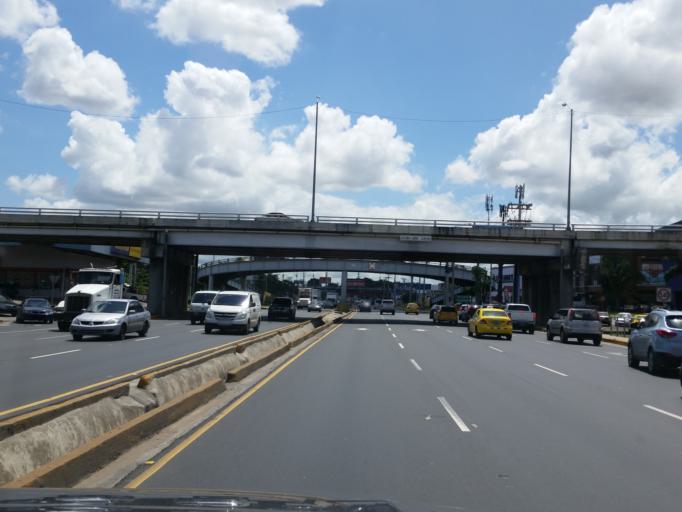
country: PA
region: Panama
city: San Miguelito
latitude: 9.0501
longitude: -79.4547
